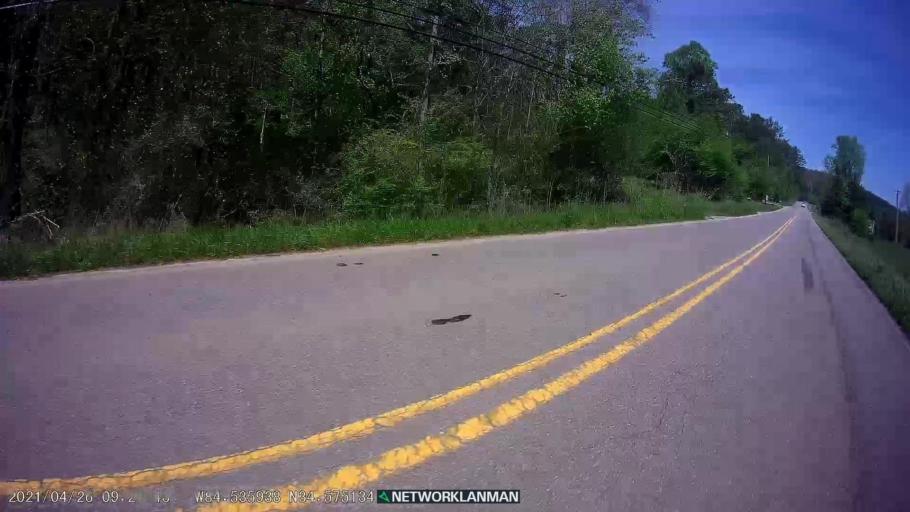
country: US
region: Georgia
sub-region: Gilmer County
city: Ellijay
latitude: 34.5753
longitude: -84.5359
